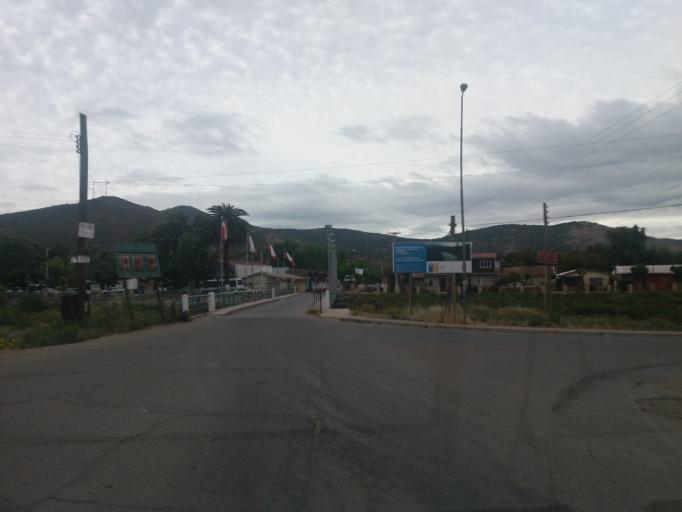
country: CL
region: Valparaiso
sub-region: Provincia de Quillota
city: Hacienda La Calera
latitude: -32.7315
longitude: -71.2015
